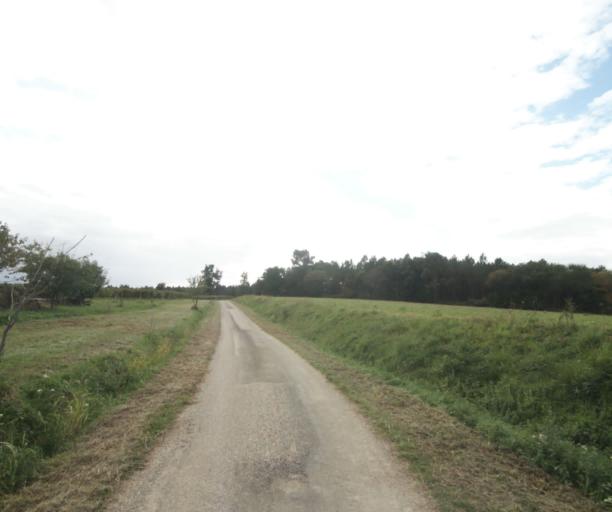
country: FR
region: Midi-Pyrenees
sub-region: Departement du Gers
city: Eauze
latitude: 43.9173
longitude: 0.1058
